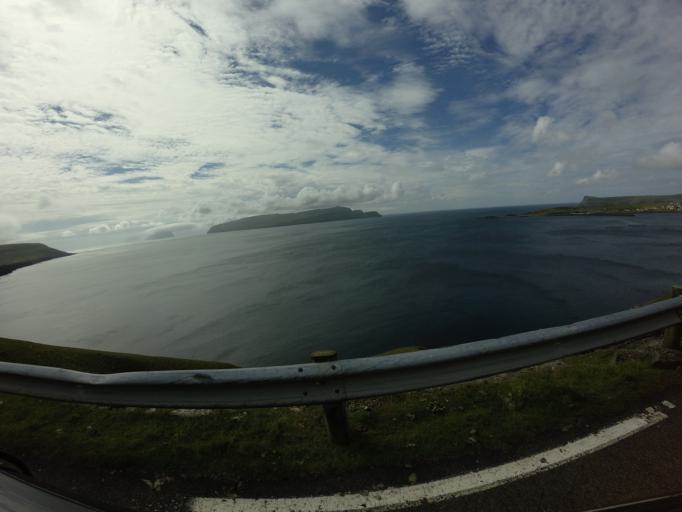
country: FO
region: Sandoy
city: Sandur
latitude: 61.8323
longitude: -6.7785
